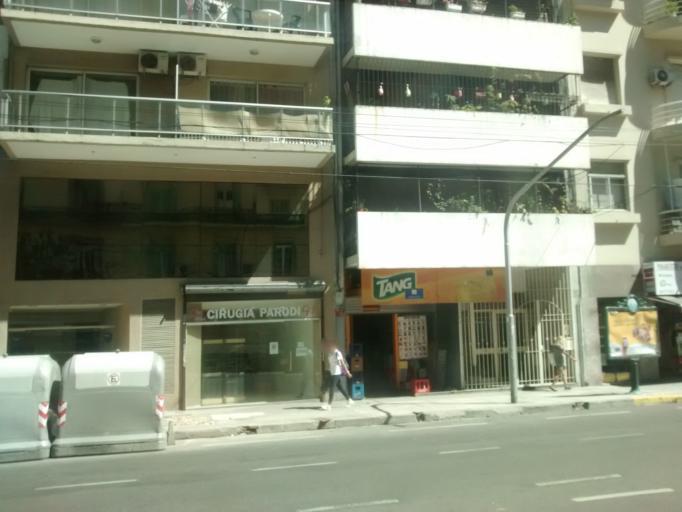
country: AR
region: Buenos Aires F.D.
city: Retiro
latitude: -34.5996
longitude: -58.4016
